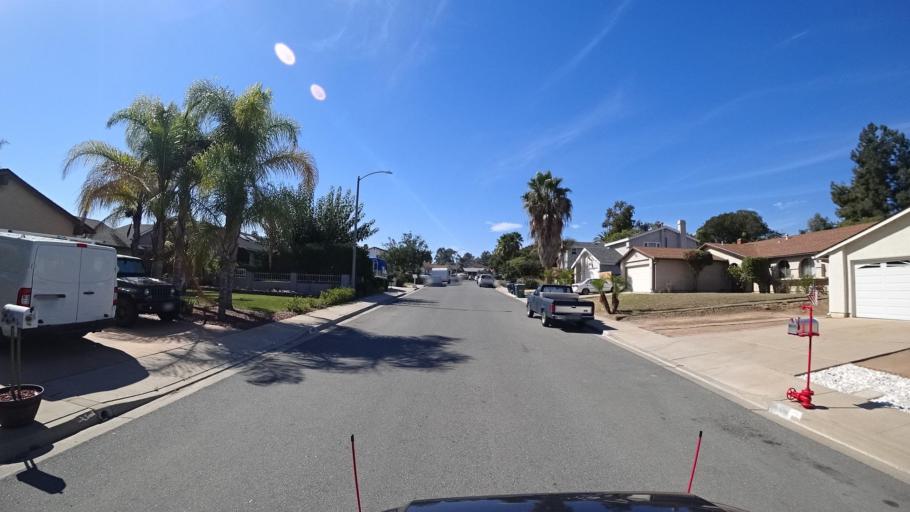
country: US
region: California
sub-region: San Diego County
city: La Presa
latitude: 32.7034
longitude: -116.9952
